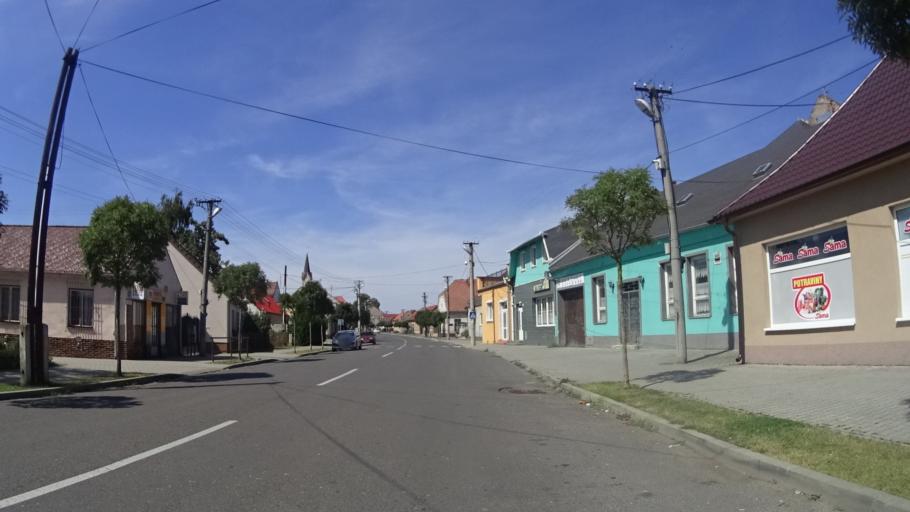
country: AT
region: Lower Austria
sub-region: Politischer Bezirk Ganserndorf
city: Marchegg
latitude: 48.3280
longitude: 16.9093
